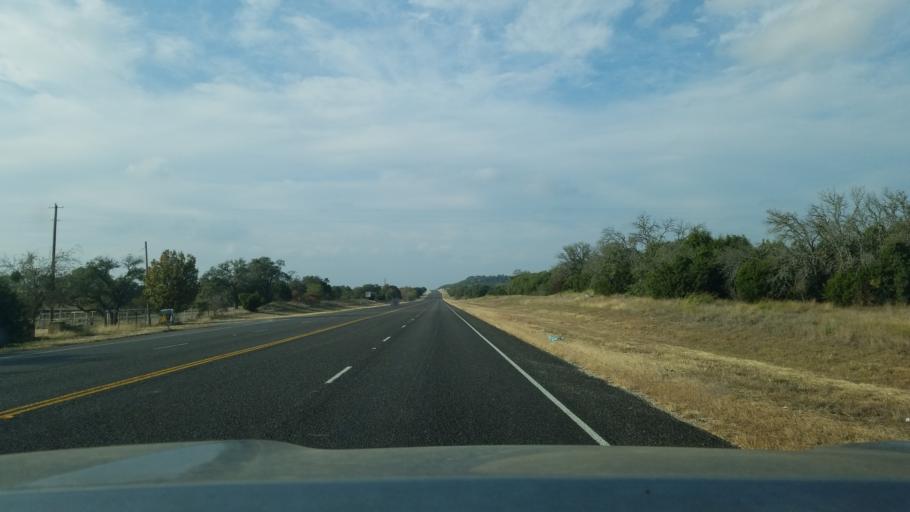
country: US
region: Texas
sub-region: Mills County
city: Goldthwaite
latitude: 31.2466
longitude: -98.4266
